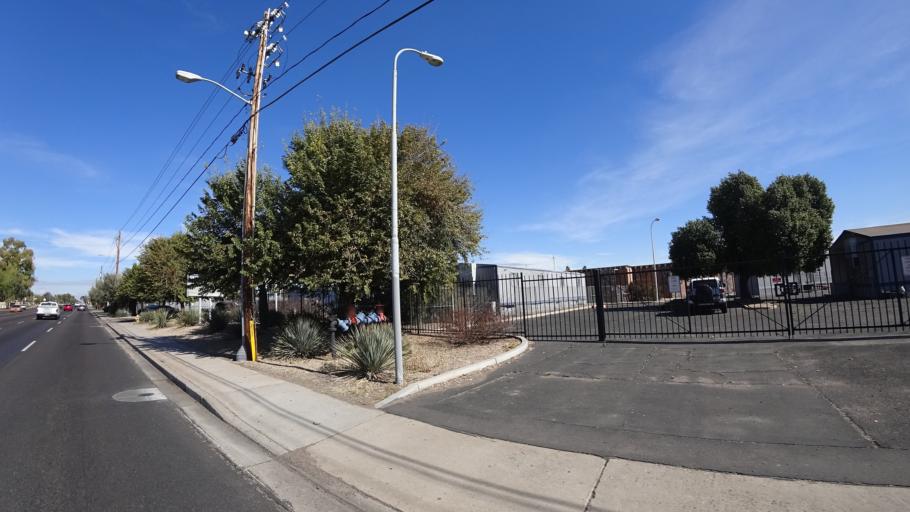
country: US
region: Arizona
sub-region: Maricopa County
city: Glendale
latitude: 33.4964
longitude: -112.2031
